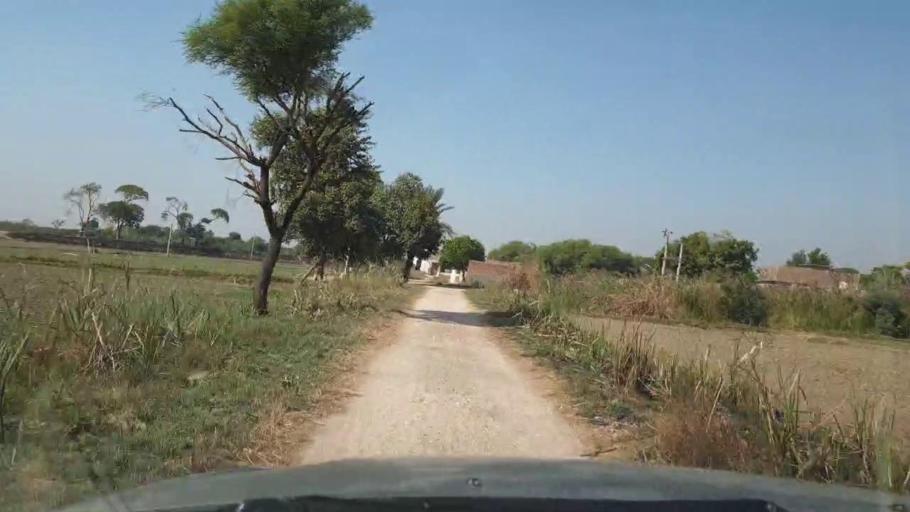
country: PK
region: Sindh
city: Tando Muhammad Khan
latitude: 24.9920
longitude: 68.4998
